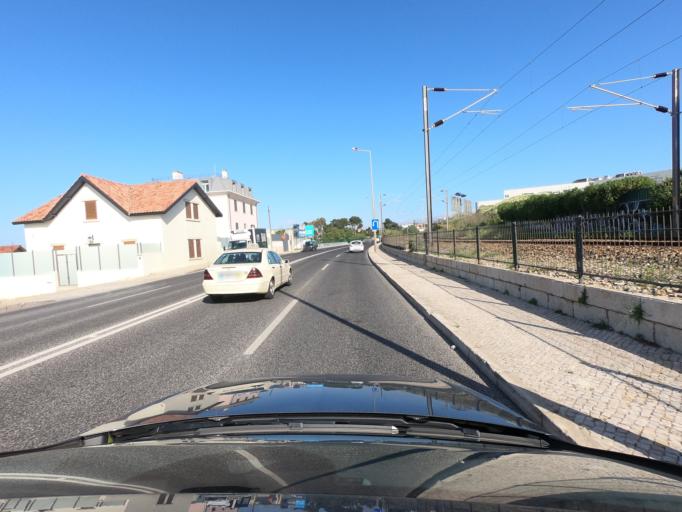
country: PT
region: Lisbon
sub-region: Cascais
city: Estoril
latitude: 38.6973
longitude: -9.3808
